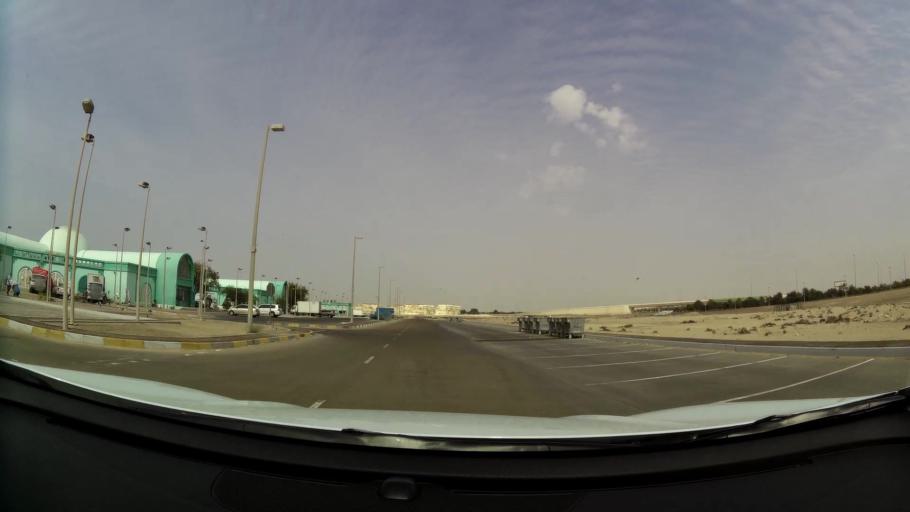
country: AE
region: Abu Dhabi
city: Abu Dhabi
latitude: 24.5436
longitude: 54.6862
